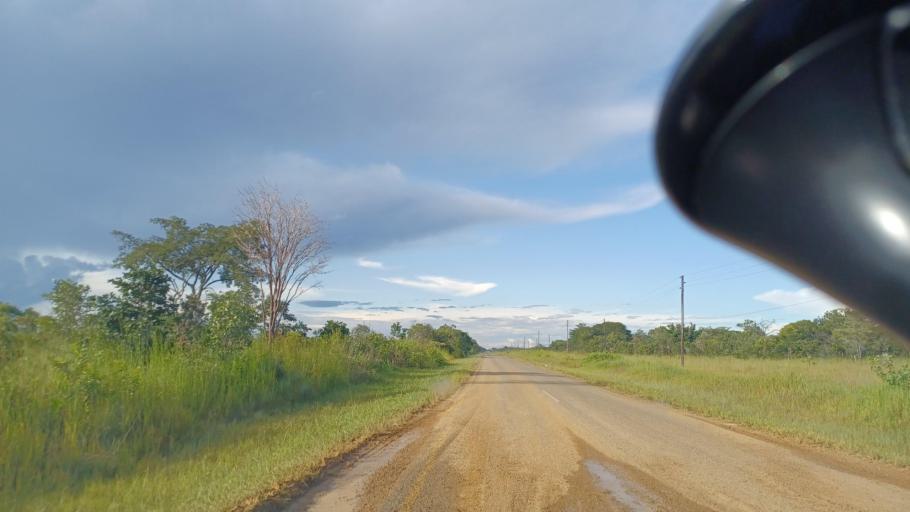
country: ZM
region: North-Western
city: Kabompo
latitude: -13.2858
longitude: 24.4773
